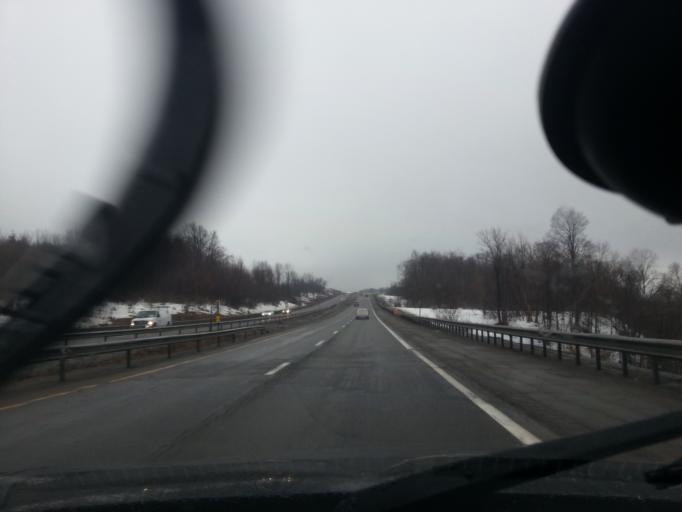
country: US
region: New York
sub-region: Onondaga County
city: Nedrow
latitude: 42.8669
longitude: -76.1140
